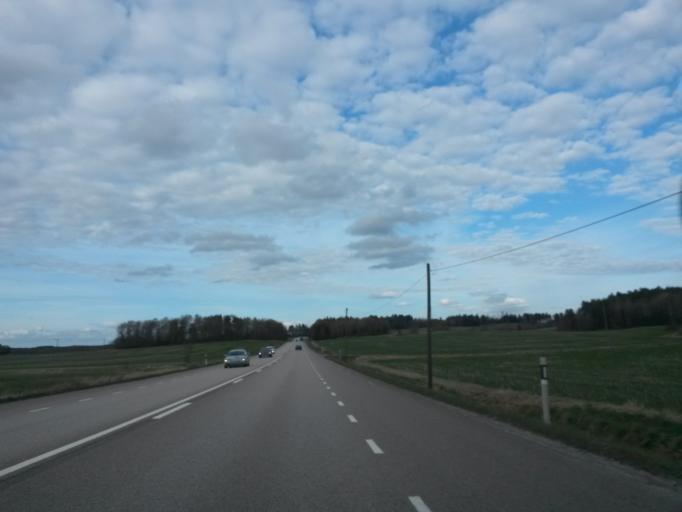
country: SE
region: Vaestra Goetaland
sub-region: Alingsas Kommun
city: Alingsas
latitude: 57.9582
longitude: 12.6140
